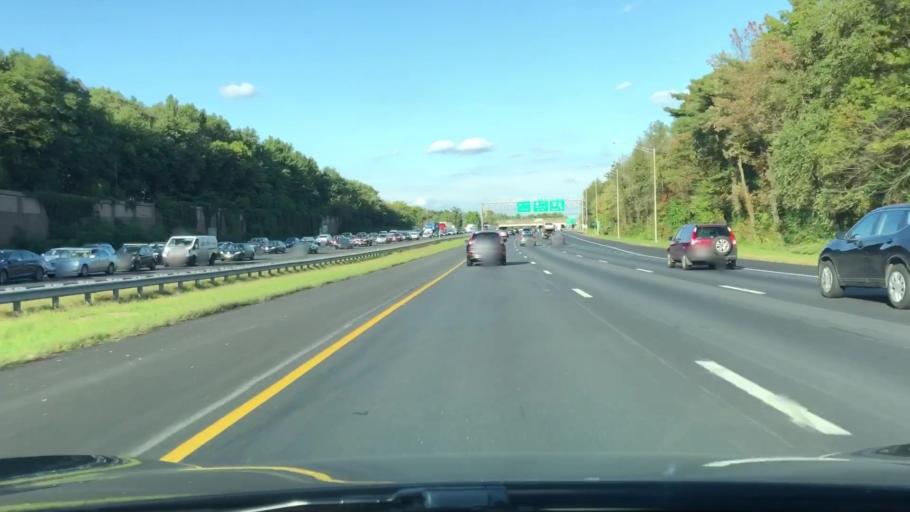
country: US
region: New Jersey
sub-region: Camden County
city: Kingston Estates
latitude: 39.9312
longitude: -74.9706
